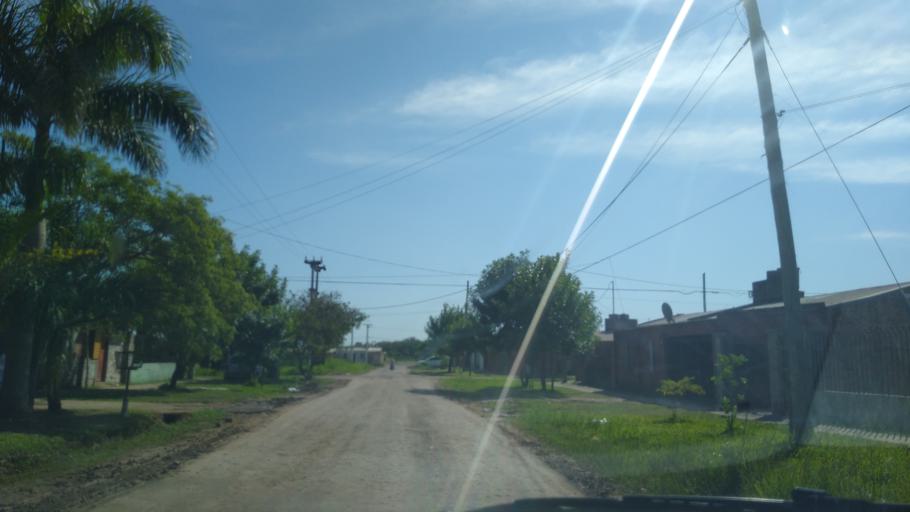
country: AR
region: Chaco
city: Barranqueras
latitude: -27.4955
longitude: -58.9630
